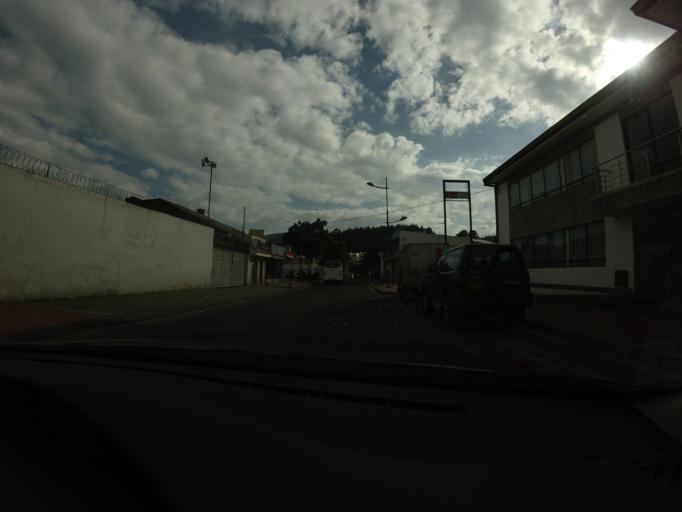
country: CO
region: Cundinamarca
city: Zipaquira
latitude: 5.0198
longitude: -74.0041
